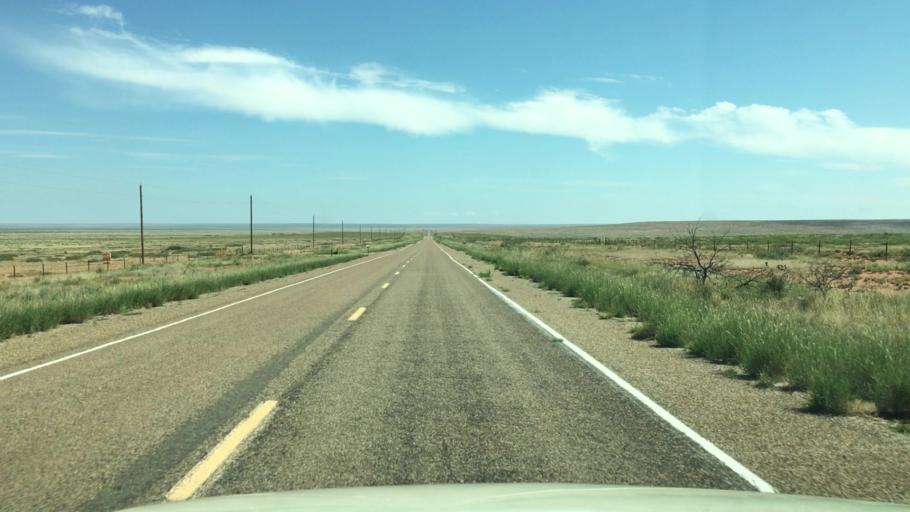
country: US
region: New Mexico
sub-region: De Baca County
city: Fort Sumner
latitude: 33.9906
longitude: -104.5705
